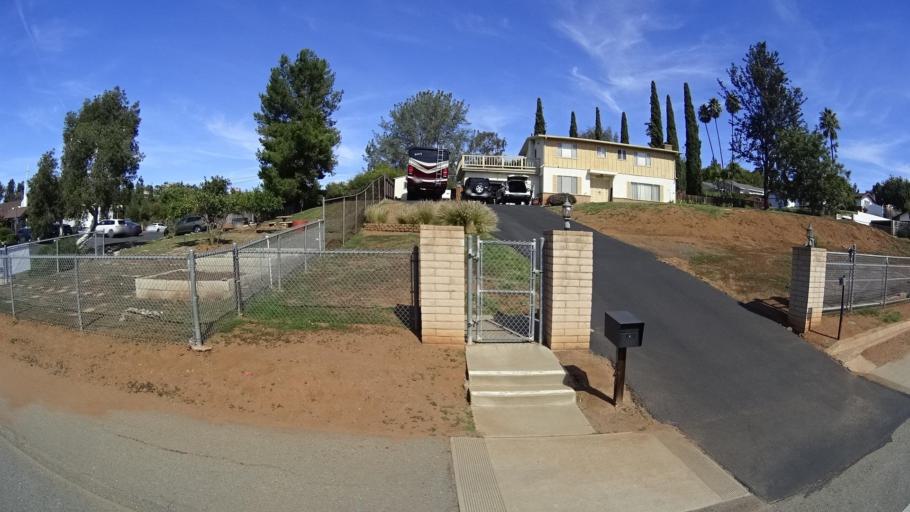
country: US
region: California
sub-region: San Diego County
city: Casa de Oro-Mount Helix
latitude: 32.7513
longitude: -116.9603
